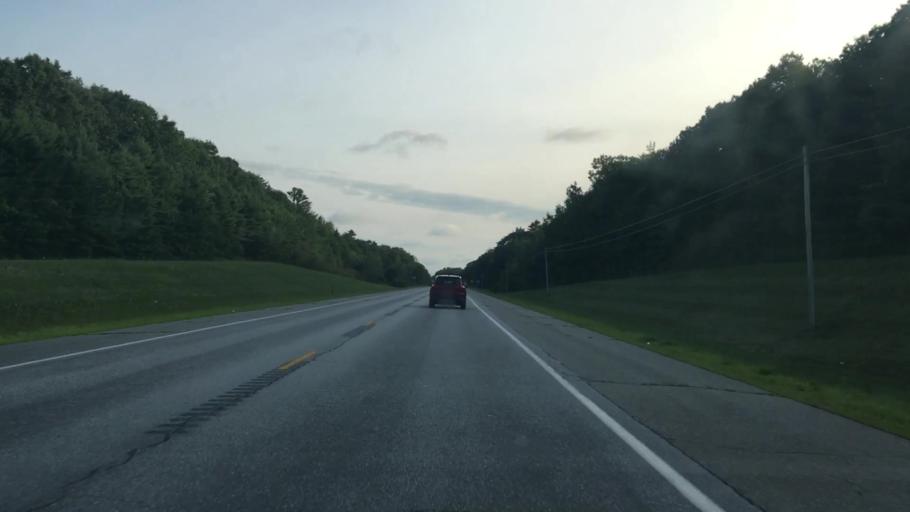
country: US
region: Maine
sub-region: Lincoln County
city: Nobleboro
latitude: 44.0666
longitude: -69.4884
